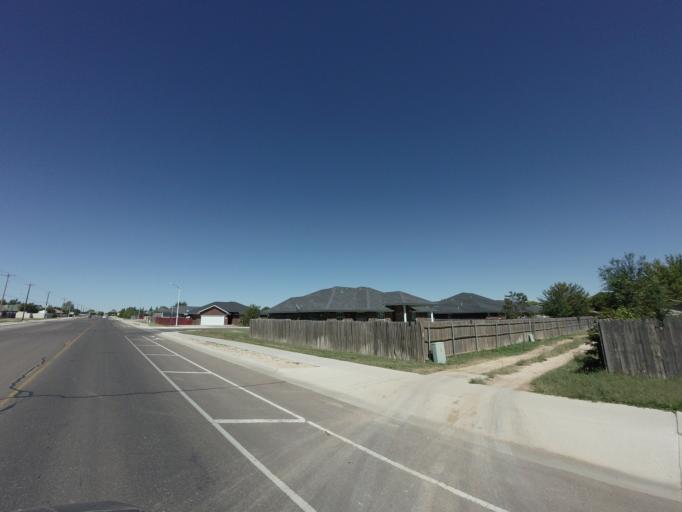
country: US
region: New Mexico
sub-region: Curry County
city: Clovis
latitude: 34.4430
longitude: -103.1784
